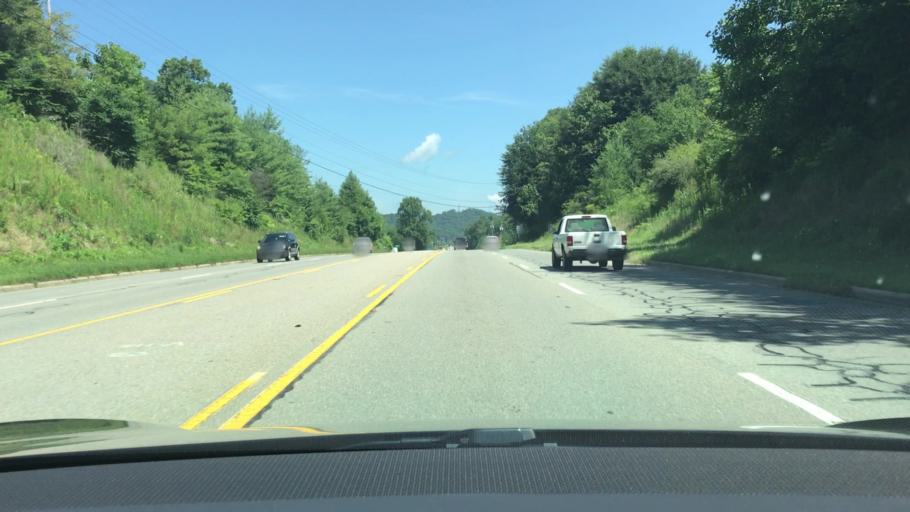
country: US
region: North Carolina
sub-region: Macon County
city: Franklin
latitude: 35.1165
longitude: -83.3909
